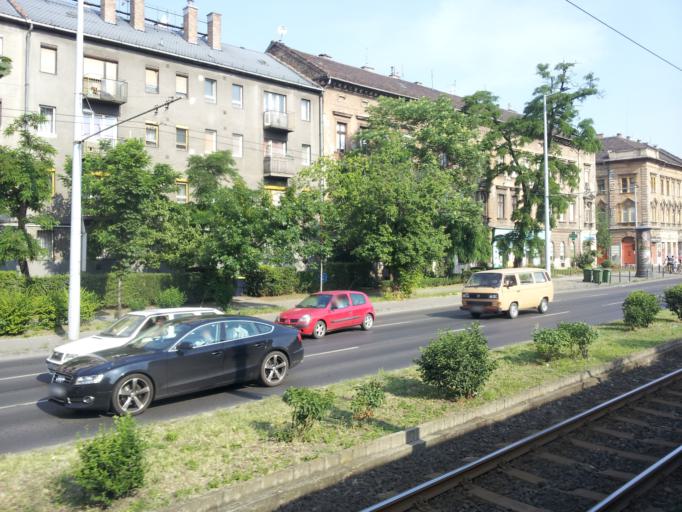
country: HU
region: Budapest
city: Budapest XIV. keruelet
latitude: 47.4927
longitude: 19.1089
